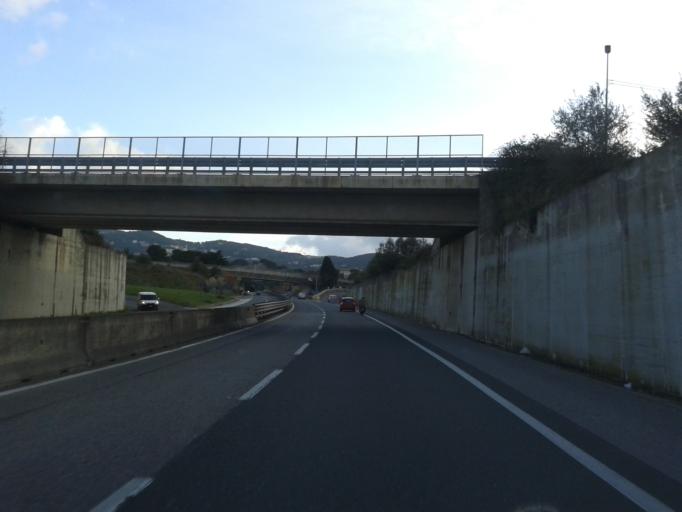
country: IT
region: Tuscany
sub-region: Provincia di Livorno
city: Livorno
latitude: 43.5141
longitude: 10.3326
